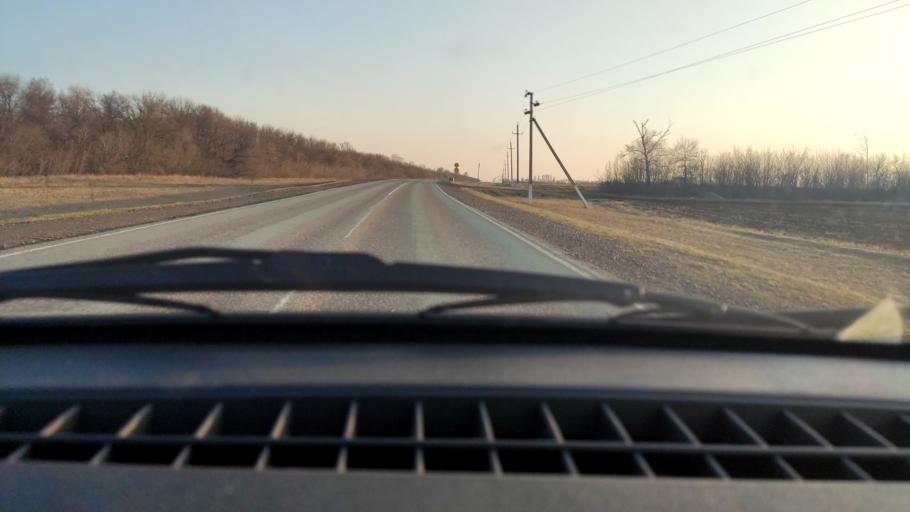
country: RU
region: Bashkortostan
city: Davlekanovo
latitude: 54.3291
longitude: 55.1651
